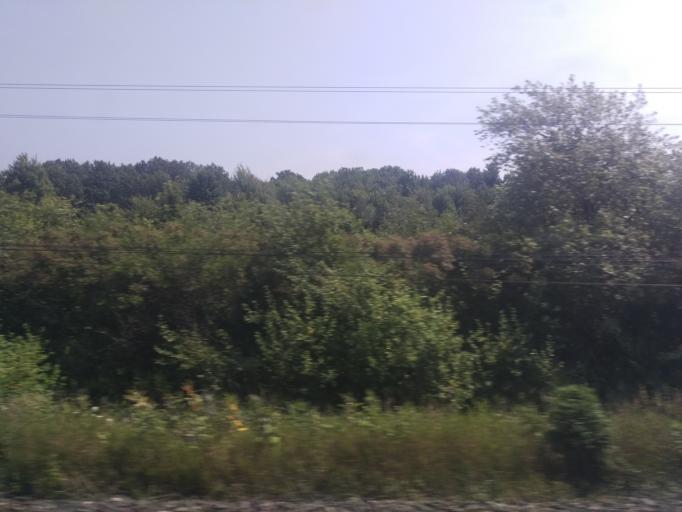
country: CA
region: Ontario
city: Gananoque
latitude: 44.3412
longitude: -76.2842
